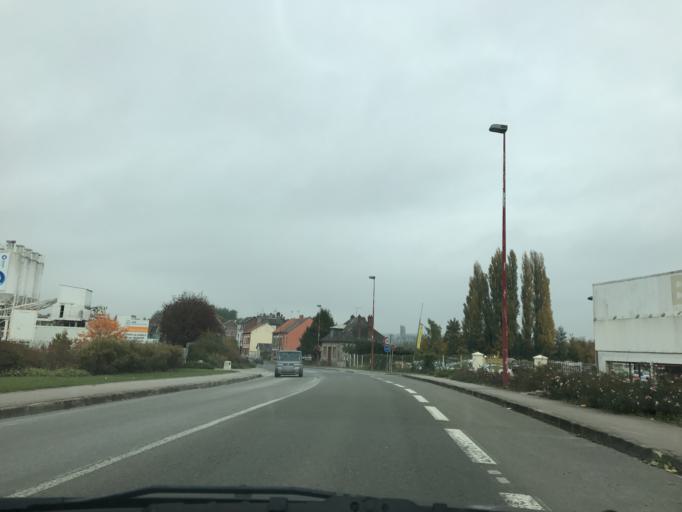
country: FR
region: Picardie
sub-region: Departement de la Somme
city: Peronne
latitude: 49.9195
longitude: 2.9341
